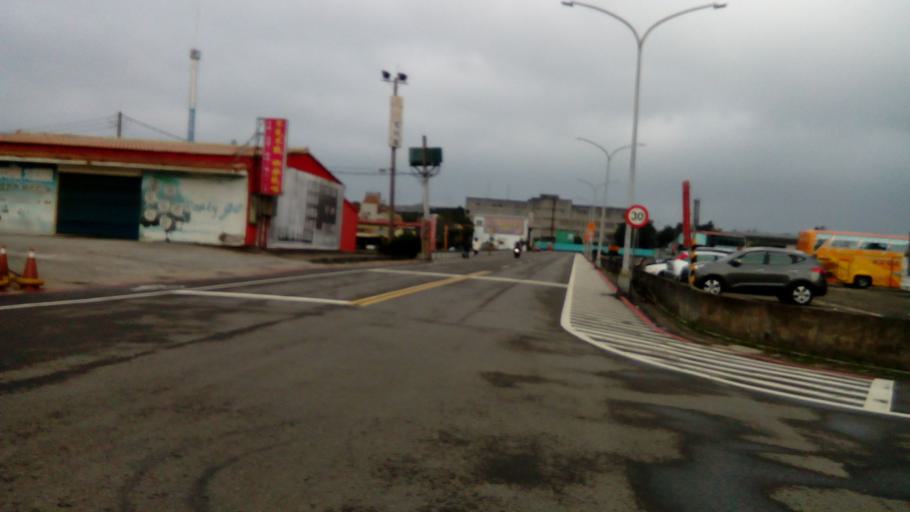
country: TW
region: Taipei
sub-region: Taipei
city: Banqiao
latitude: 25.1802
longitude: 121.4199
